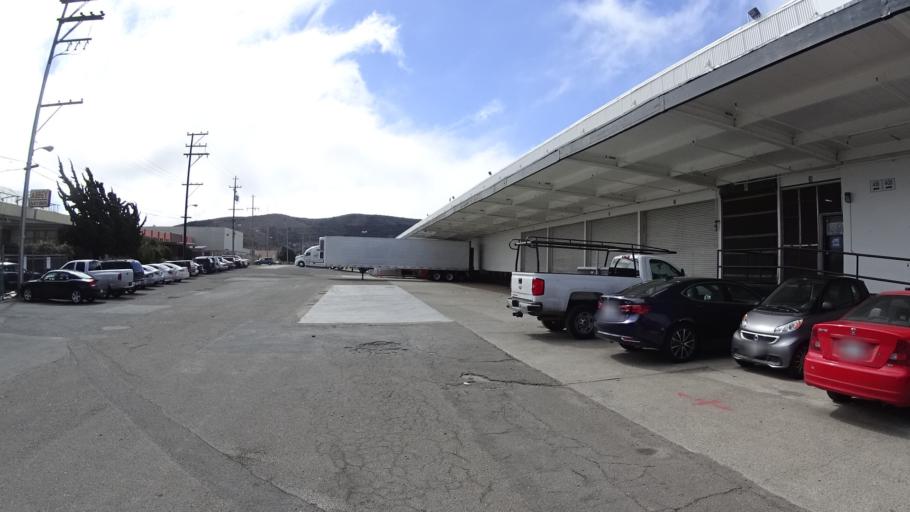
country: US
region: California
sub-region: San Mateo County
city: Brisbane
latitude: 37.7088
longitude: -122.4101
